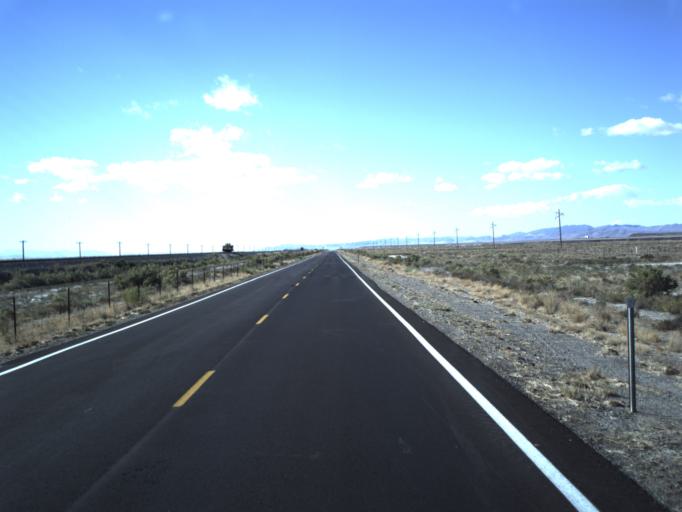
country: US
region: Utah
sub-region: Millard County
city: Delta
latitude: 39.2201
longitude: -112.6756
